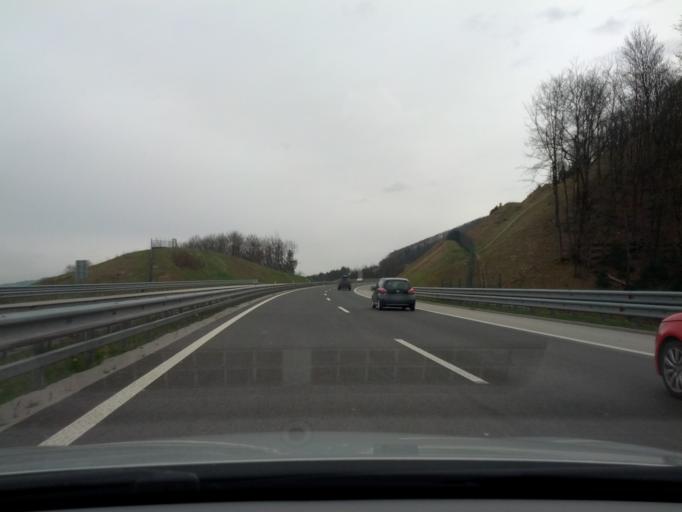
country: SI
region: Trebnje
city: Trebnje
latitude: 45.9043
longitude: 14.9862
